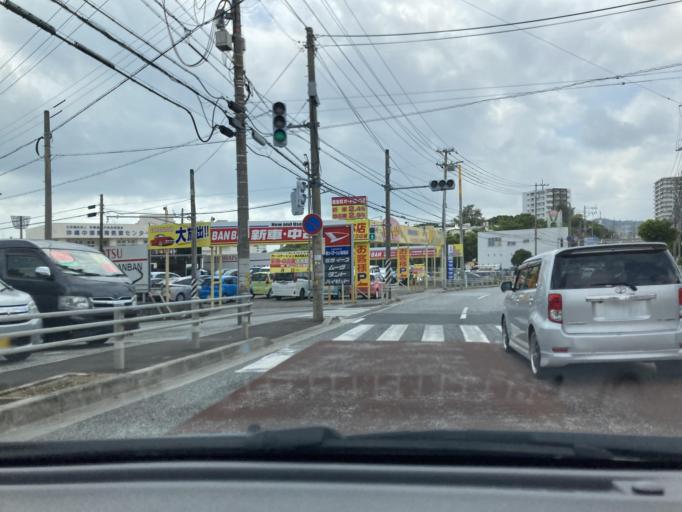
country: JP
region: Okinawa
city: Okinawa
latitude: 26.3142
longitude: 127.8190
